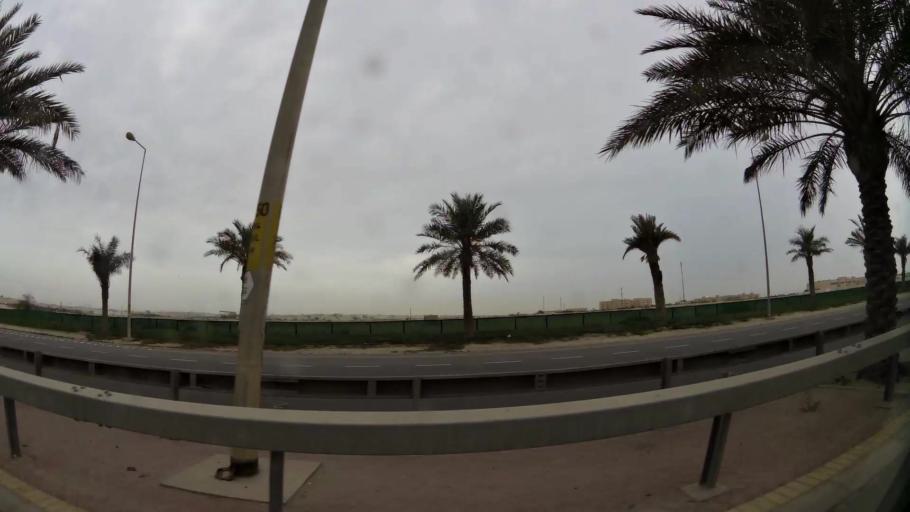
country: BH
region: Northern
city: Ar Rifa'
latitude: 26.1032
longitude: 50.5421
